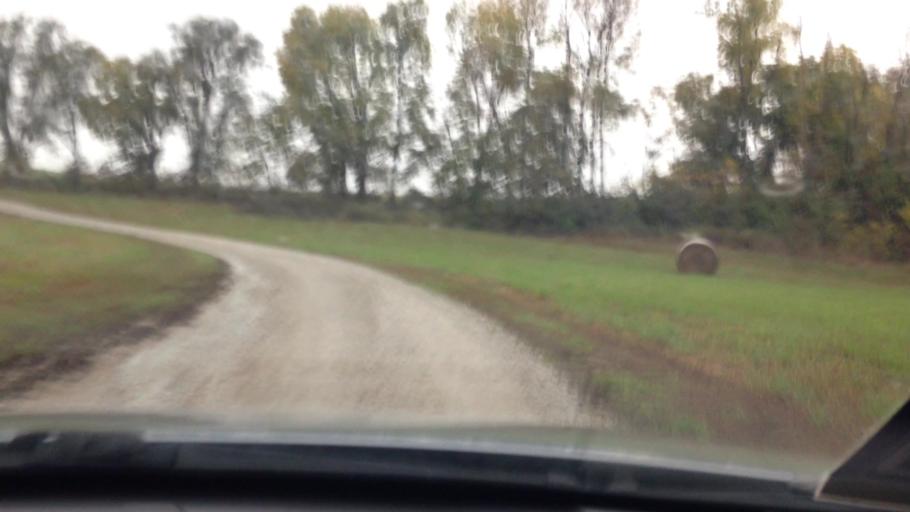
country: US
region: Missouri
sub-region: Platte County
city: Weston
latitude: 39.3885
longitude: -94.8499
